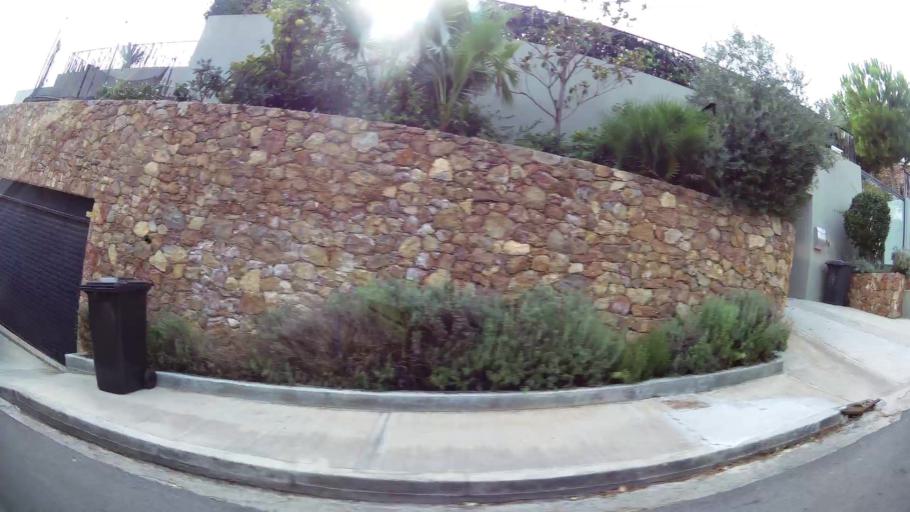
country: GR
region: Attica
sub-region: Nomarchia Athinas
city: Filothei
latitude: 38.0277
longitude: 23.7701
